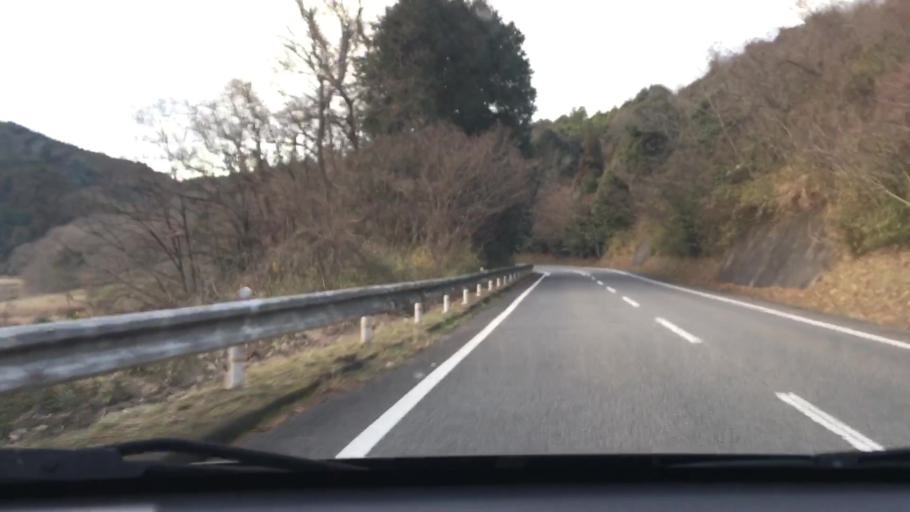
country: JP
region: Oita
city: Hiji
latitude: 33.4125
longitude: 131.4240
